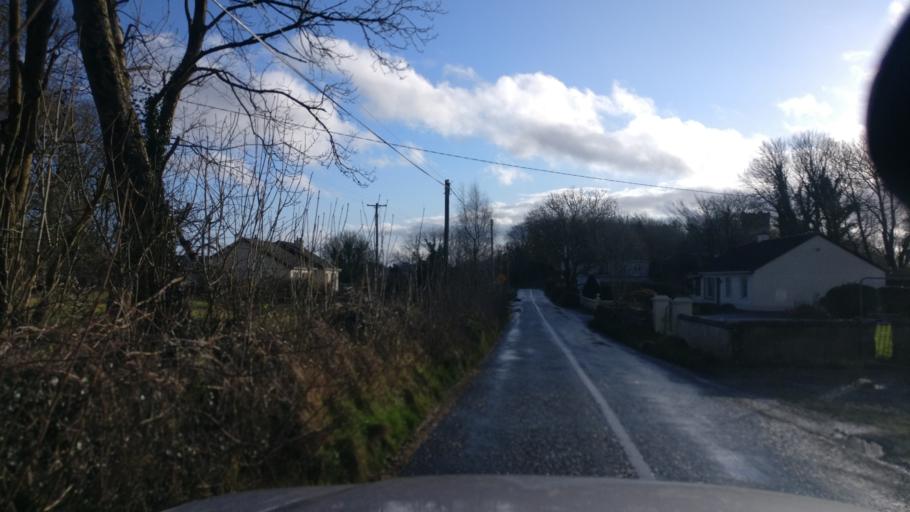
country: IE
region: Connaught
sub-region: County Galway
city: Loughrea
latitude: 53.2583
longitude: -8.6261
